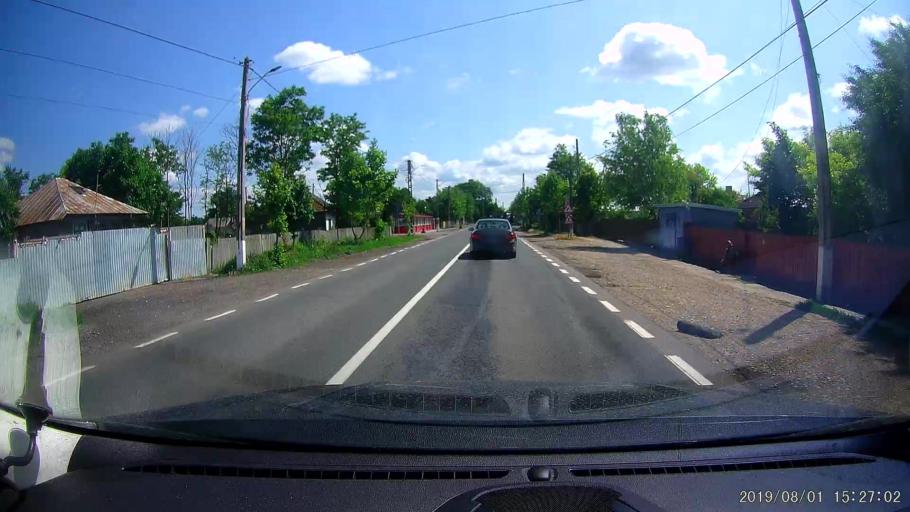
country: RO
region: Braila
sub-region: Comuna Viziru
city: Viziru
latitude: 45.0045
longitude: 27.7172
